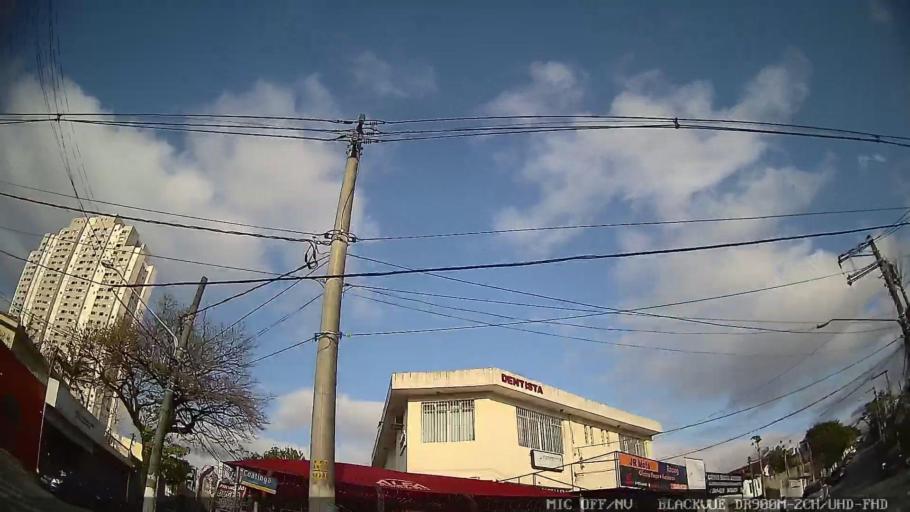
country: BR
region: Sao Paulo
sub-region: Taboao Da Serra
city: Taboao da Serra
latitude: -23.6210
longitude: -46.7576
